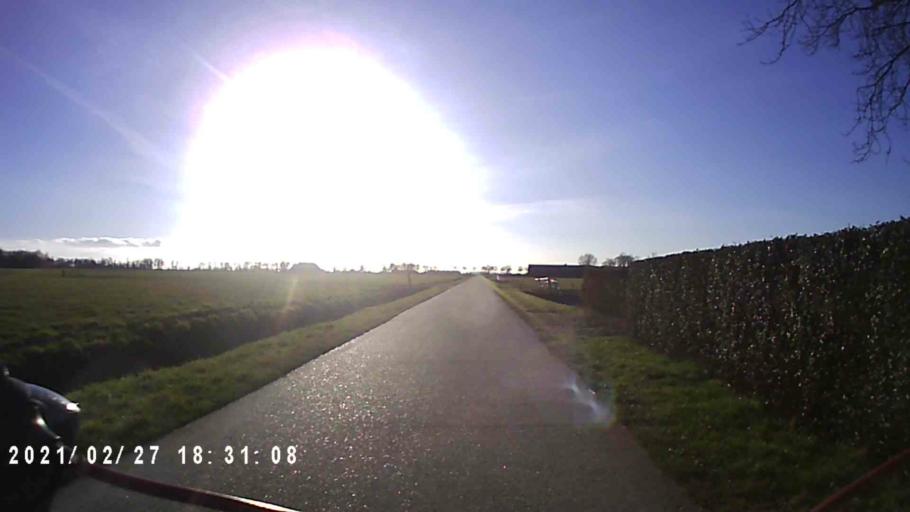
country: NL
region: Groningen
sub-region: Gemeente Winsum
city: Winsum
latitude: 53.3135
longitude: 6.5405
